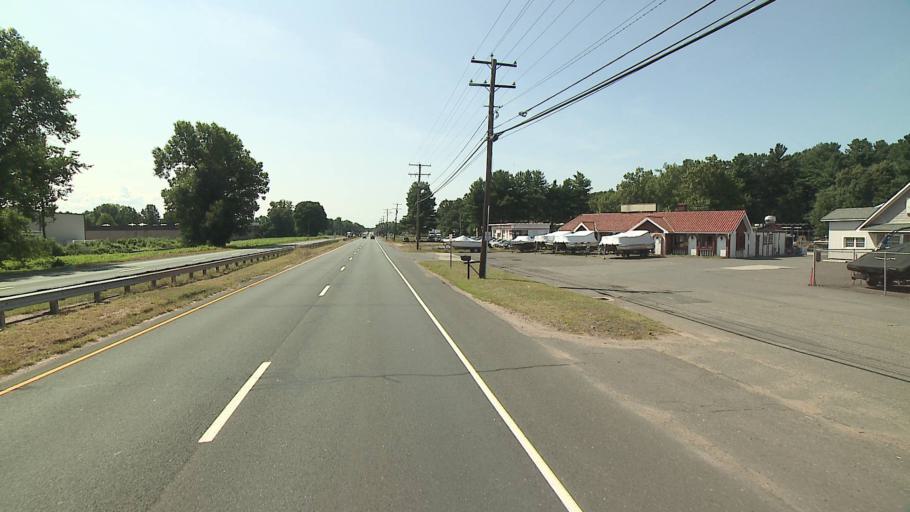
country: US
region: Connecticut
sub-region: Hartford County
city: South Windsor
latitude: 41.8231
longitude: -72.6081
